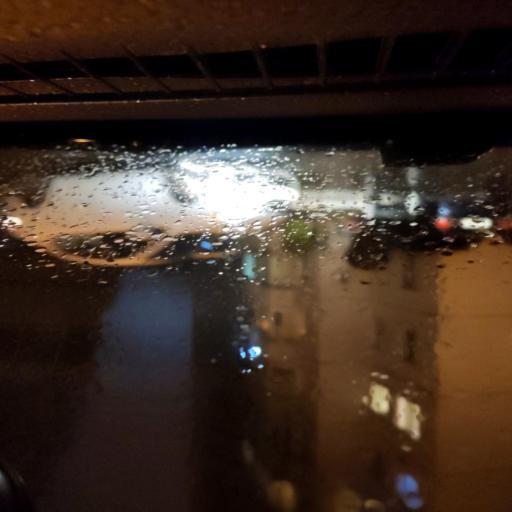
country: RU
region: Voronezj
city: Podgornoye
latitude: 51.7249
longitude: 39.1651
